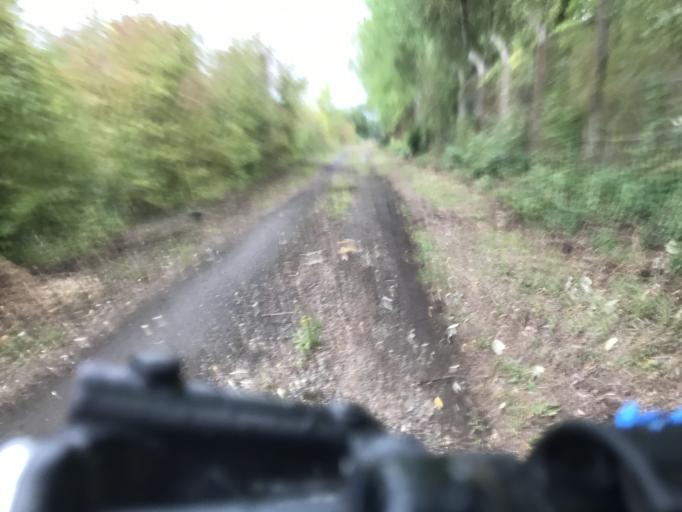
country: FR
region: Picardie
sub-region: Departement de l'Oise
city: Saint-Maximin
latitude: 49.2306
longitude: 2.4418
